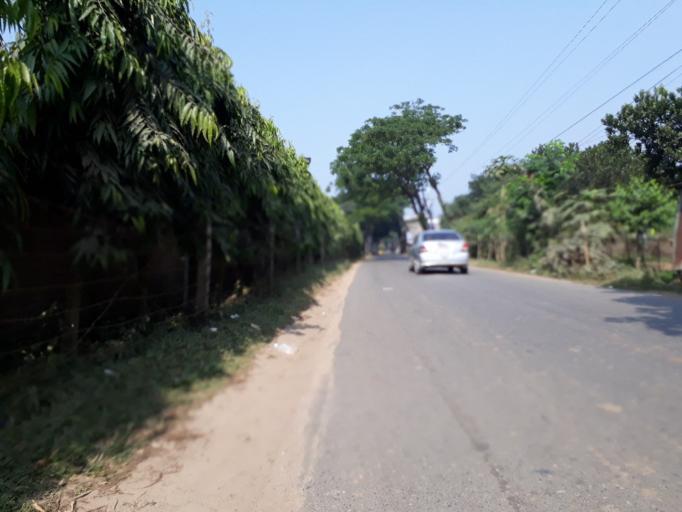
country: BD
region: Dhaka
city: Tungi
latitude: 23.8645
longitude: 90.3107
